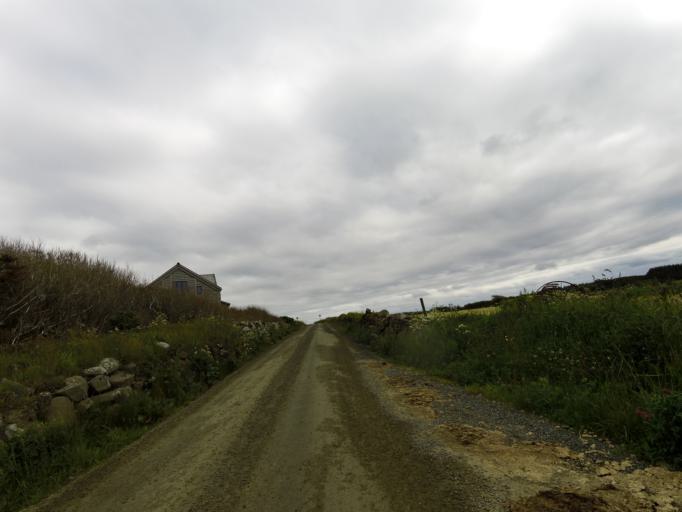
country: NO
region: Vest-Agder
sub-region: Farsund
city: Vestbygd
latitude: 58.1359
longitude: 6.6066
